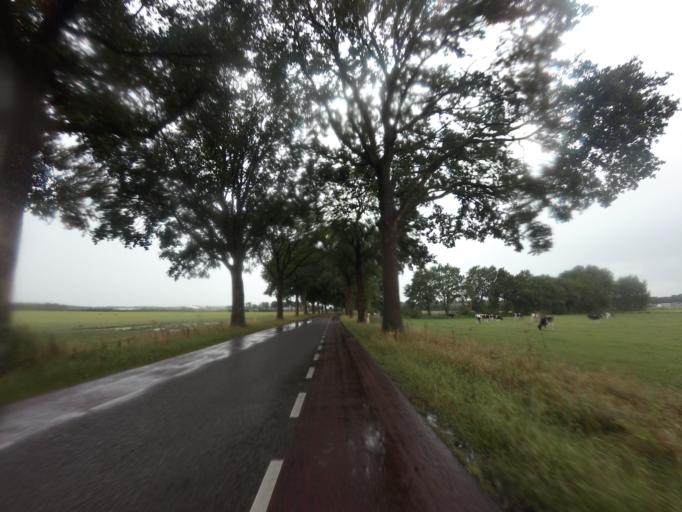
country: NL
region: Drenthe
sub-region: Gemeente Hoogeveen
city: Hoogeveen
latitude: 52.6111
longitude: 6.3956
